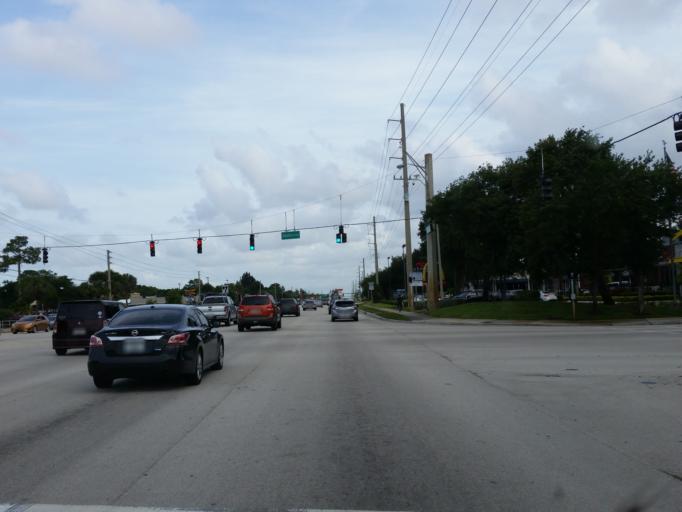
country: US
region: Florida
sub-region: Martin County
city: North River Shores
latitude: 27.2458
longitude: -80.2726
